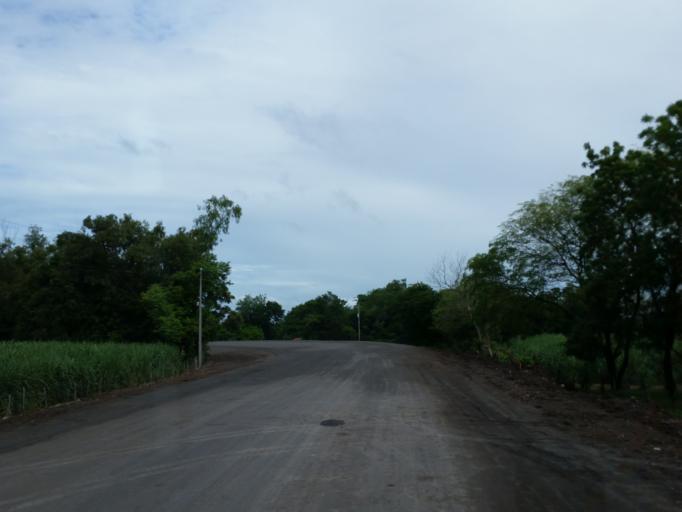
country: NI
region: Leon
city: Larreynaga
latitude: 12.5312
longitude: -86.6036
